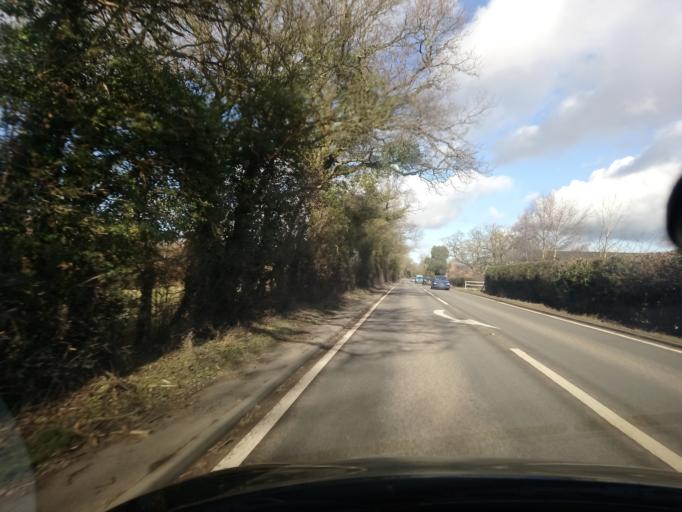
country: GB
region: England
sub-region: Shropshire
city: Astley
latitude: 52.7595
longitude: -2.7164
